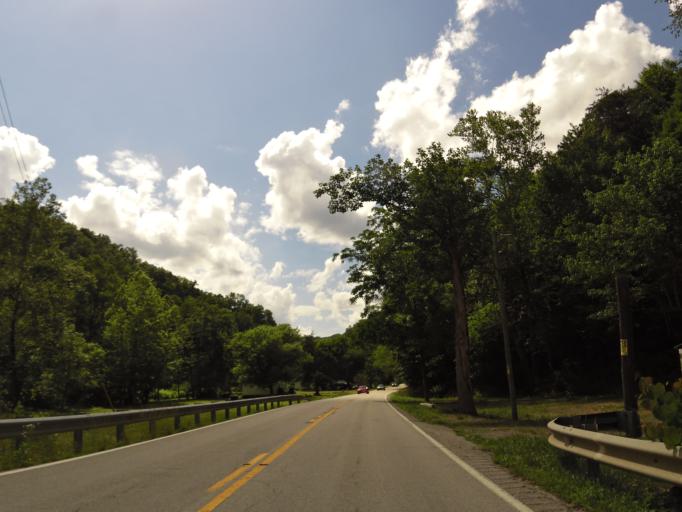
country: US
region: Virginia
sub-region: Lee County
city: Jonesville
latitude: 36.7649
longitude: -83.1504
